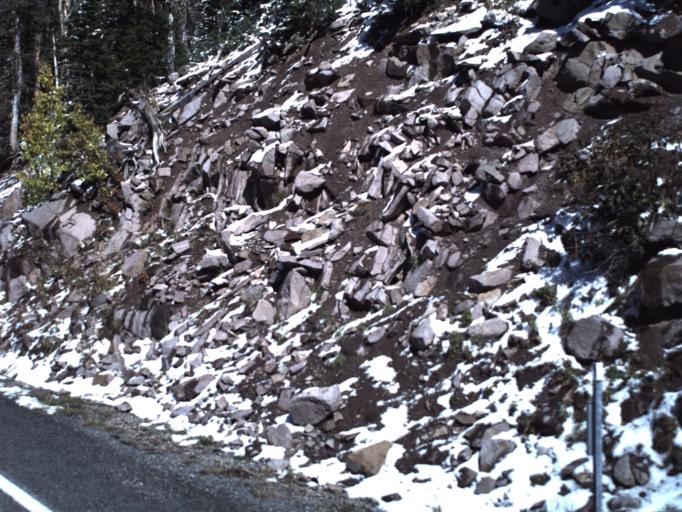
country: US
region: Utah
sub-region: Piute County
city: Junction
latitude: 38.3227
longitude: -112.3723
